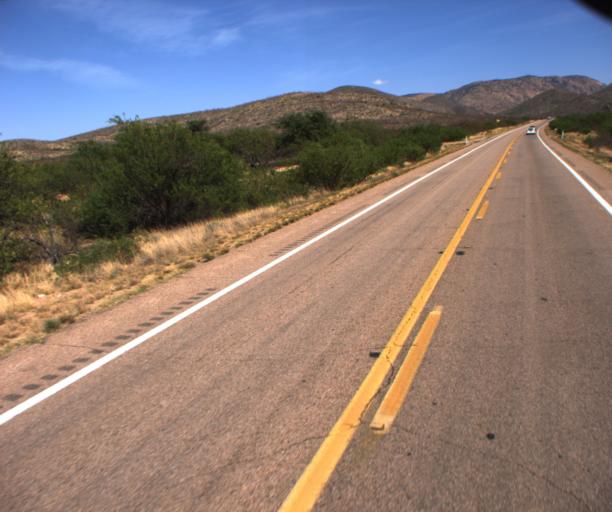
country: US
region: Arizona
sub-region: Cochise County
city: Bisbee
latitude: 31.5252
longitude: -110.0462
